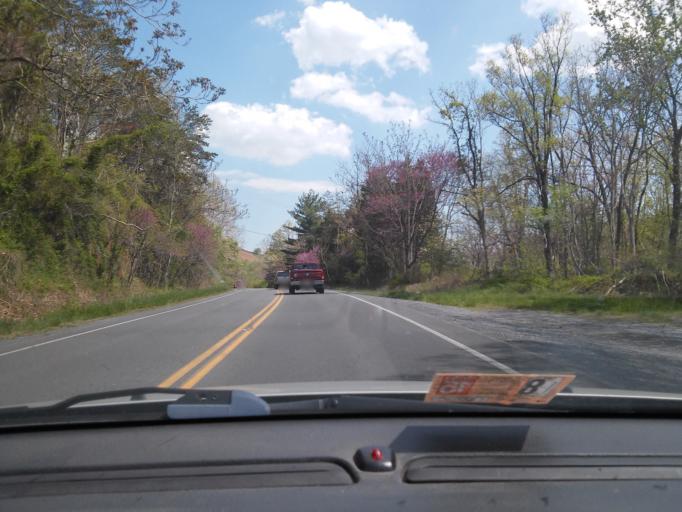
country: US
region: Virginia
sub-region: Warren County
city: Front Royal
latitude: 38.8946
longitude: -78.1784
